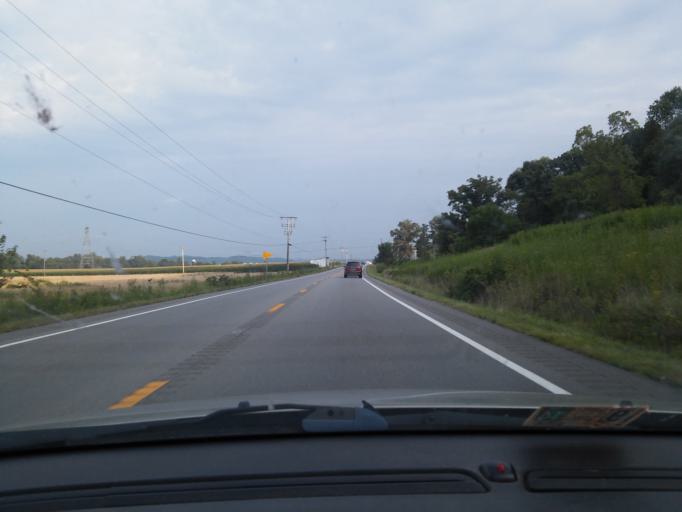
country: US
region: West Virginia
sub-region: Putnam County
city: Buffalo
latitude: 38.7504
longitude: -81.9850
